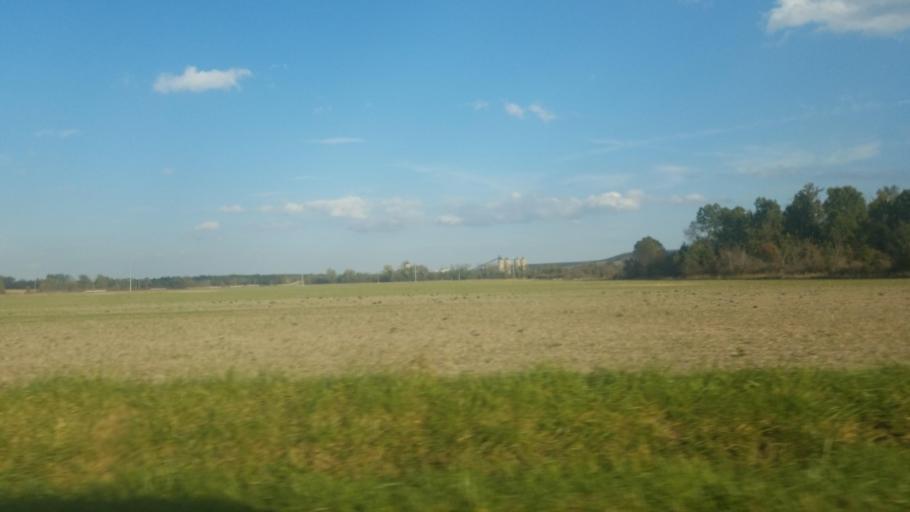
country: US
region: Illinois
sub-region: Saline County
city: Harrisburg
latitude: 37.8236
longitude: -88.6147
